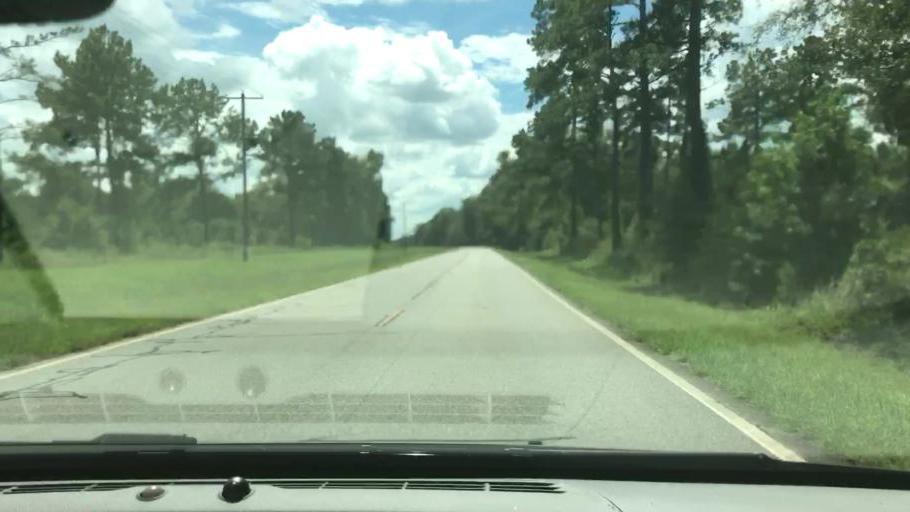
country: US
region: Georgia
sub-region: Quitman County
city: Georgetown
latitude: 32.1149
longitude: -85.0373
